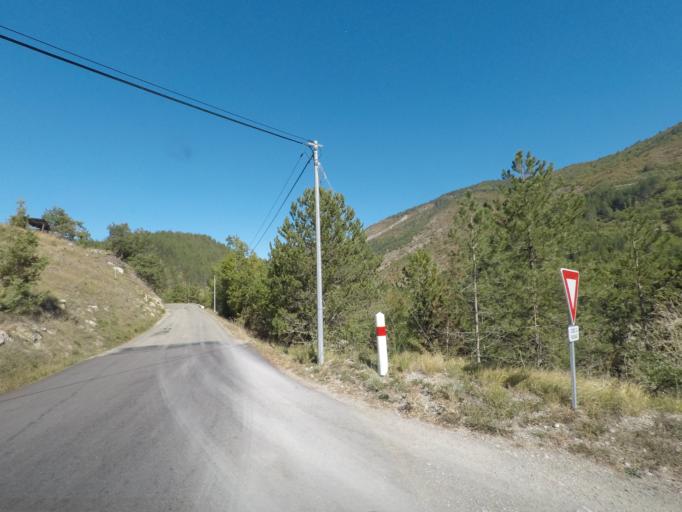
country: FR
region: Rhone-Alpes
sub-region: Departement de la Drome
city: Die
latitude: 44.6672
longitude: 5.2702
